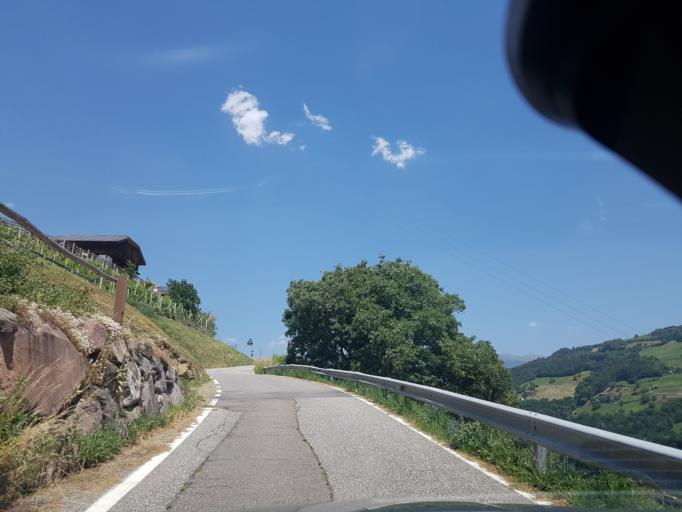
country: IT
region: Trentino-Alto Adige
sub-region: Bolzano
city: Villandro - Villanders
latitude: 46.6205
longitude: 11.5371
